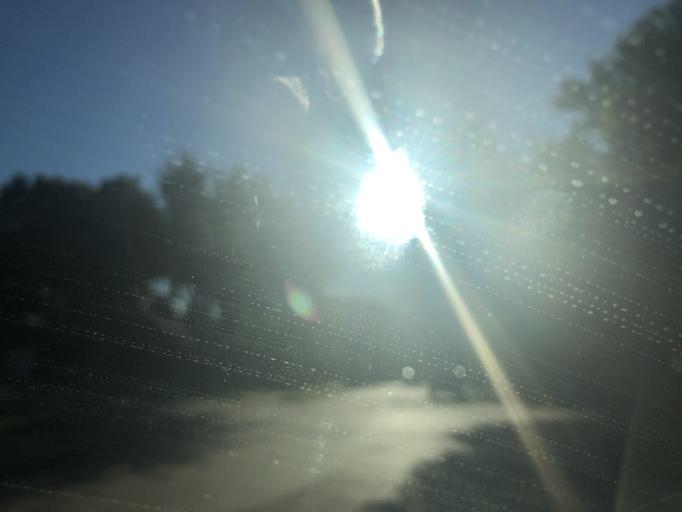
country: US
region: Texas
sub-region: Dallas County
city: Grand Prairie
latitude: 32.6655
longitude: -96.9991
